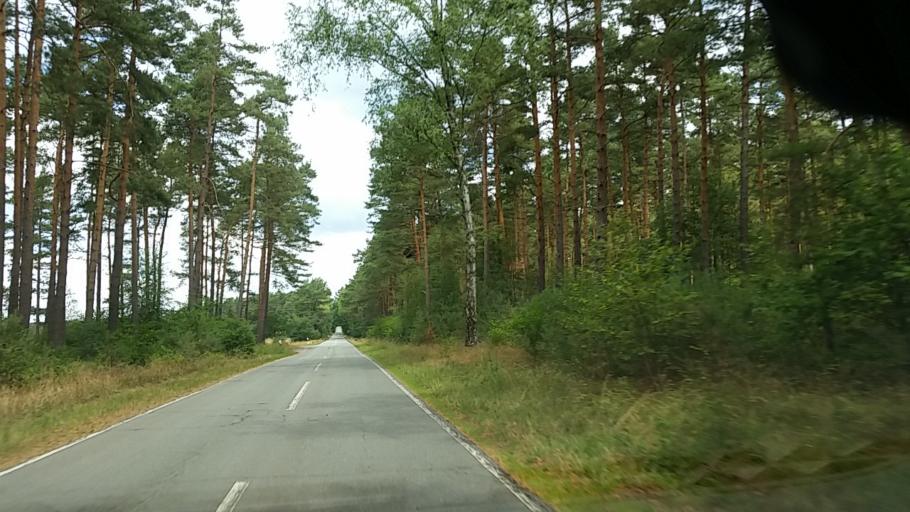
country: DE
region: Lower Saxony
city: Barwedel
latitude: 52.5846
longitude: 10.7846
